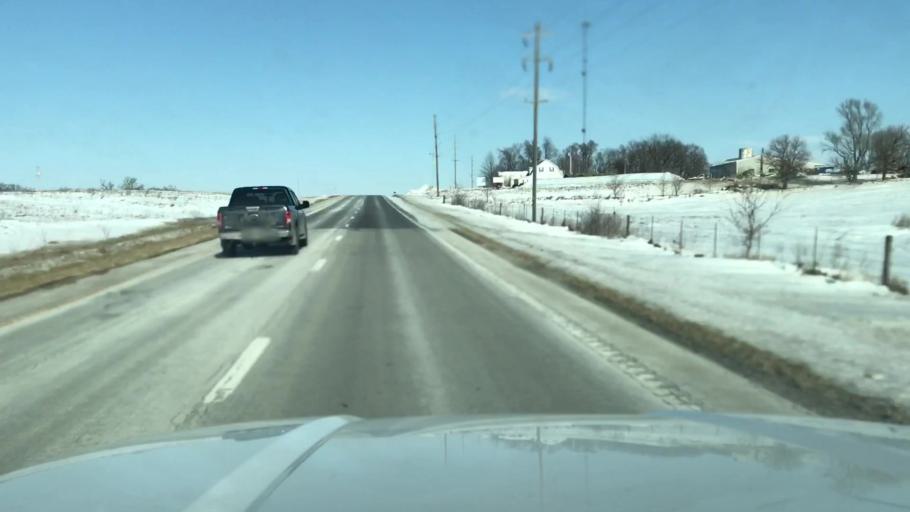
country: US
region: Missouri
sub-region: Nodaway County
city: Maryville
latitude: 40.1774
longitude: -94.8687
